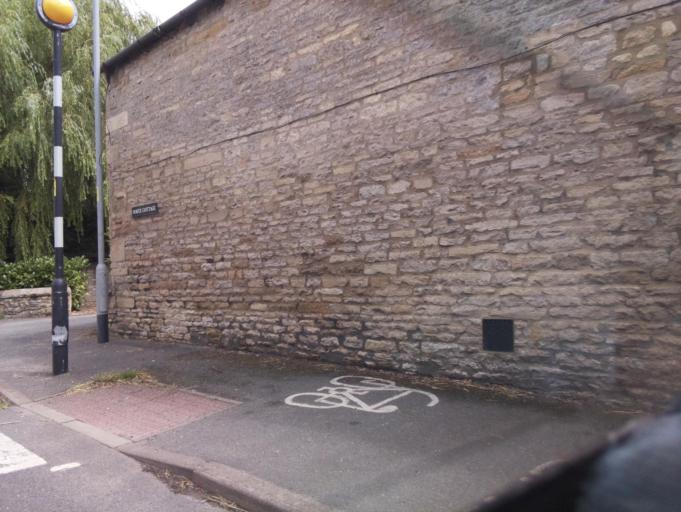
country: GB
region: England
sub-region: District of Rutland
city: Tickencote
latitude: 52.6707
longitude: -0.5222
